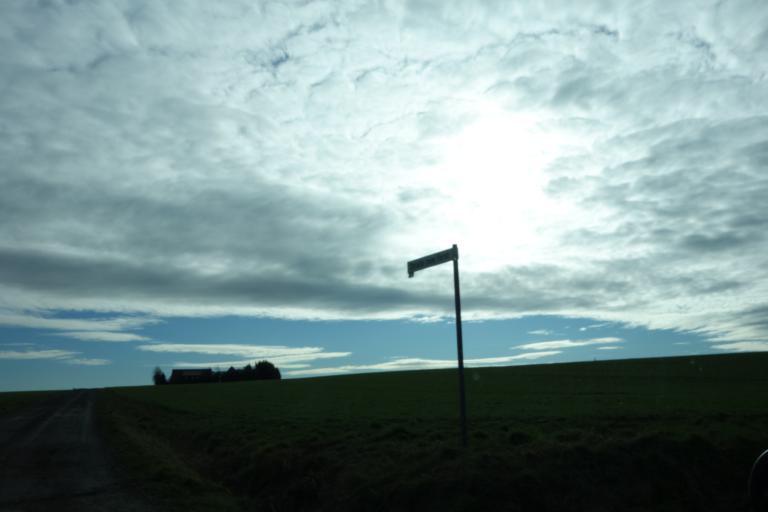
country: DE
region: Saxony
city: Reinsberg
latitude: 50.9715
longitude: 13.3714
